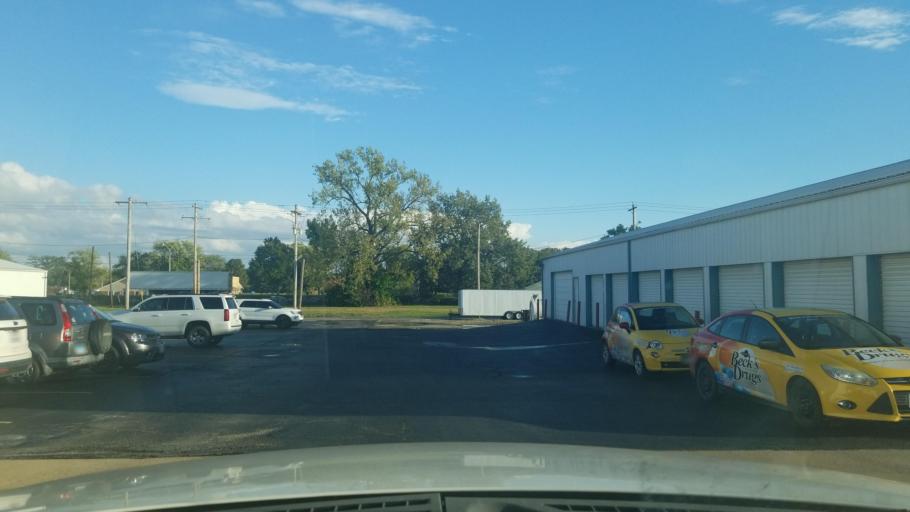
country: US
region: Illinois
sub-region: Saline County
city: Eldorado
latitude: 37.8126
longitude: -88.4402
